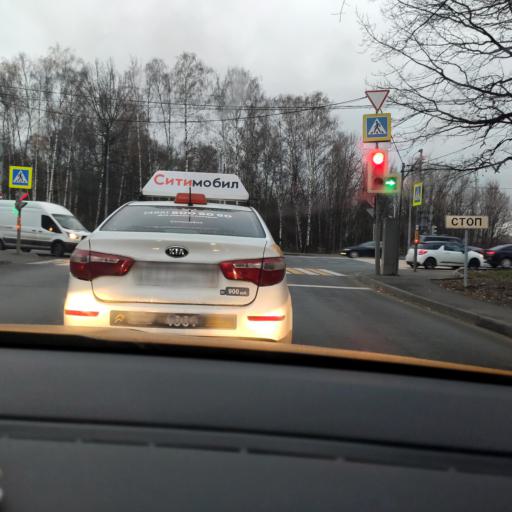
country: RU
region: Moscow
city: Vagonoremont
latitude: 55.8973
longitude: 37.5579
